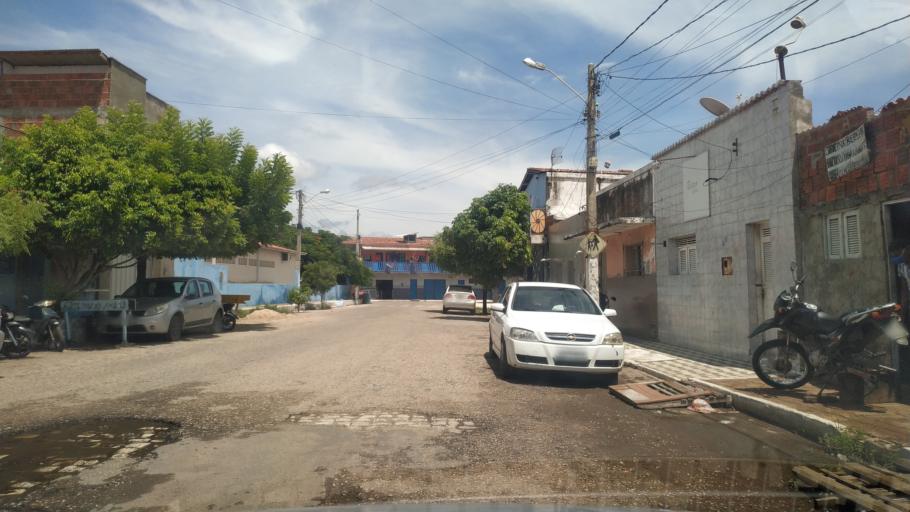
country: BR
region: Rio Grande do Norte
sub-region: Areia Branca
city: Areia Branca
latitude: -4.9557
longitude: -37.1305
